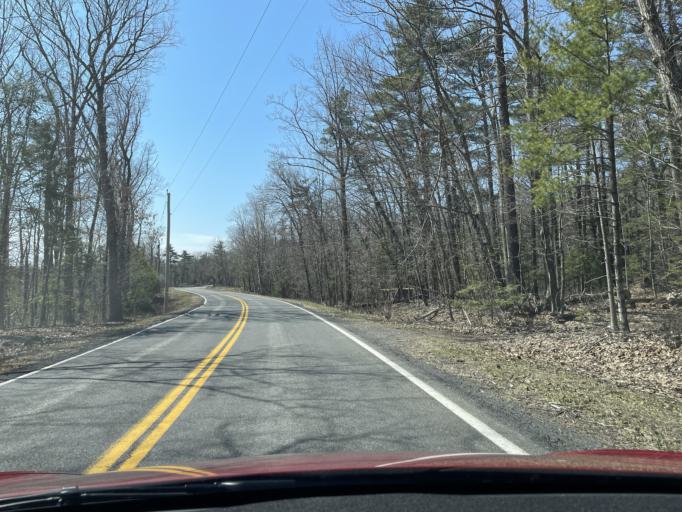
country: US
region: New York
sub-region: Ulster County
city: Zena
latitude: 42.0633
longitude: -74.0772
